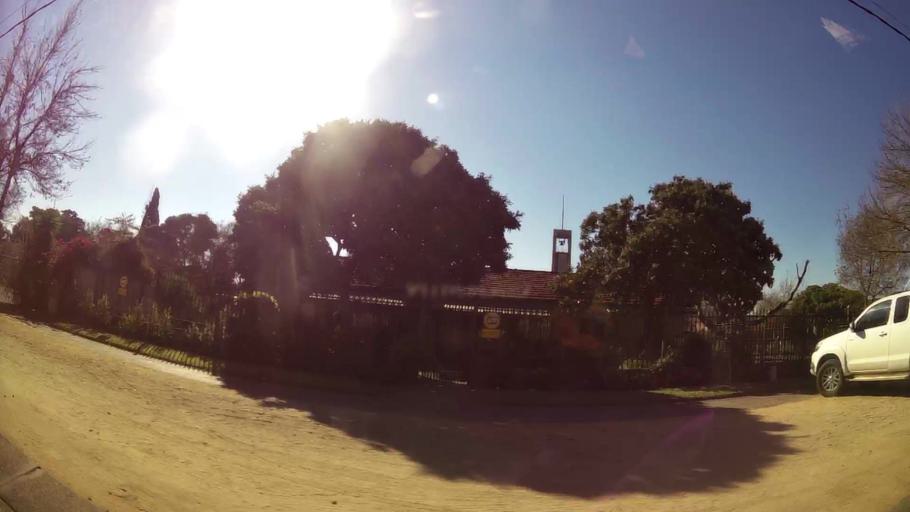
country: ZA
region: Gauteng
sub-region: City of Tshwane Metropolitan Municipality
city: Centurion
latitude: -25.8273
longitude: 28.2038
